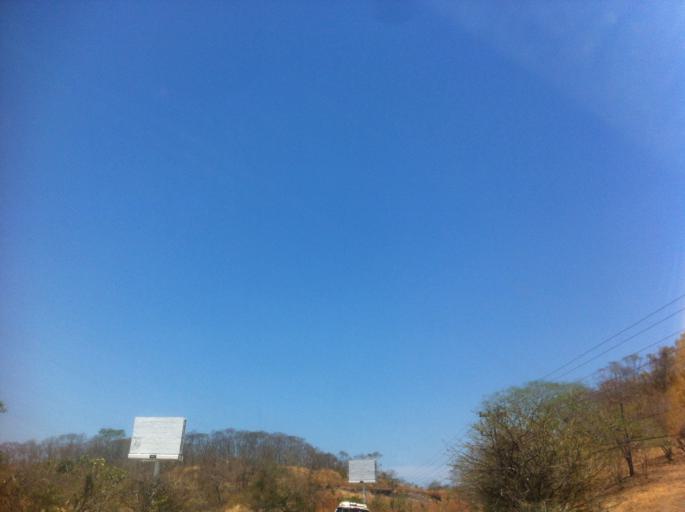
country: CR
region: Guanacaste
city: Sardinal
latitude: 10.5253
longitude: -85.5831
